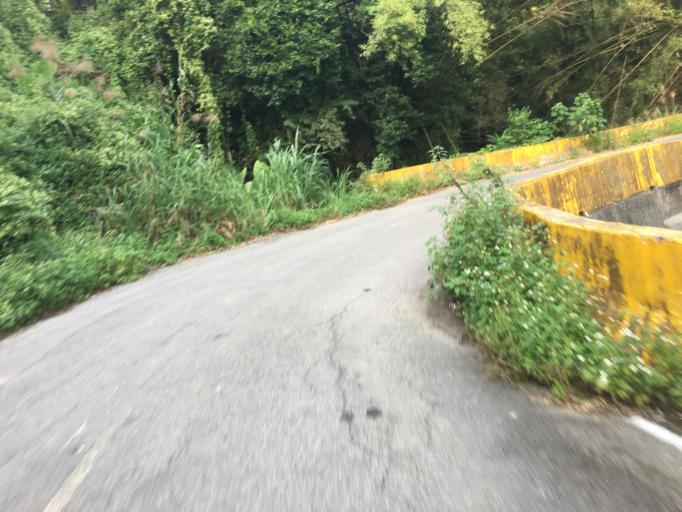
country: TW
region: Taiwan
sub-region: Hsinchu
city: Hsinchu
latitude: 24.7086
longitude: 121.0565
